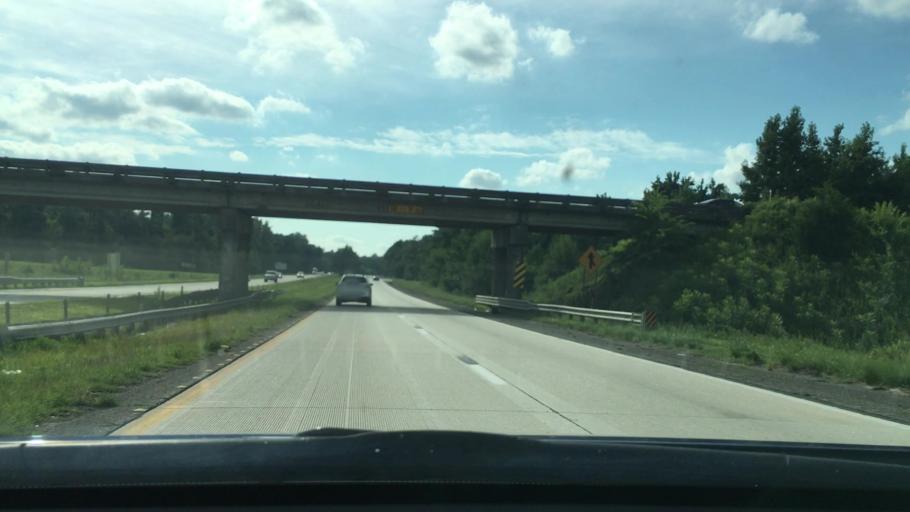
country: US
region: South Carolina
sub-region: Orangeburg County
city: Holly Hill
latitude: 33.2324
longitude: -80.4462
